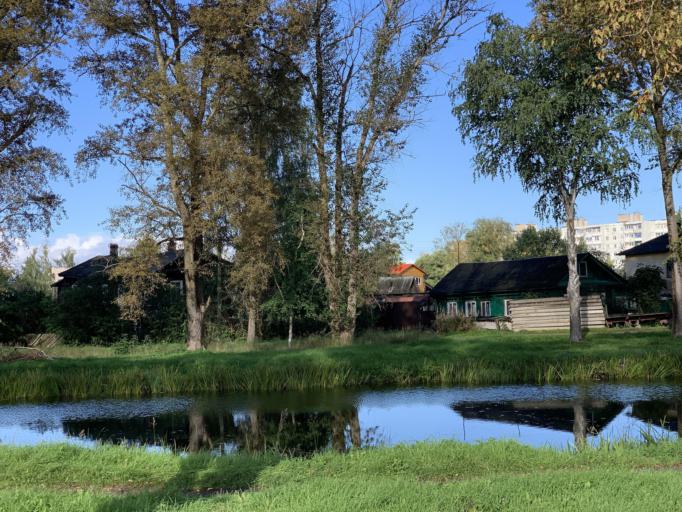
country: RU
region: Tverskaya
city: Vyshniy Volochek
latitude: 57.5863
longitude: 34.5494
